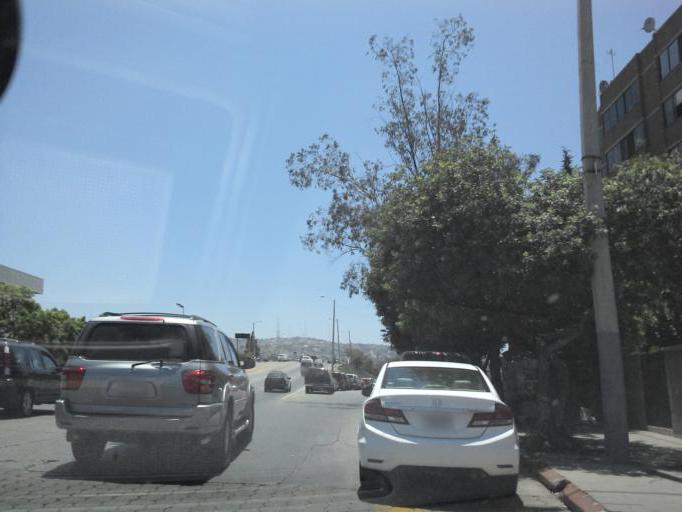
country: MX
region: Baja California
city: Tijuana
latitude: 32.5332
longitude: -117.0193
